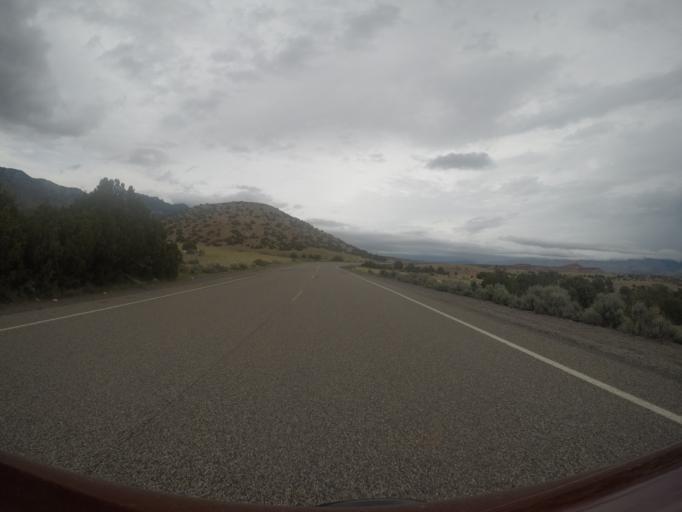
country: US
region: Wyoming
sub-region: Big Horn County
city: Lovell
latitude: 45.0649
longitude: -108.2566
